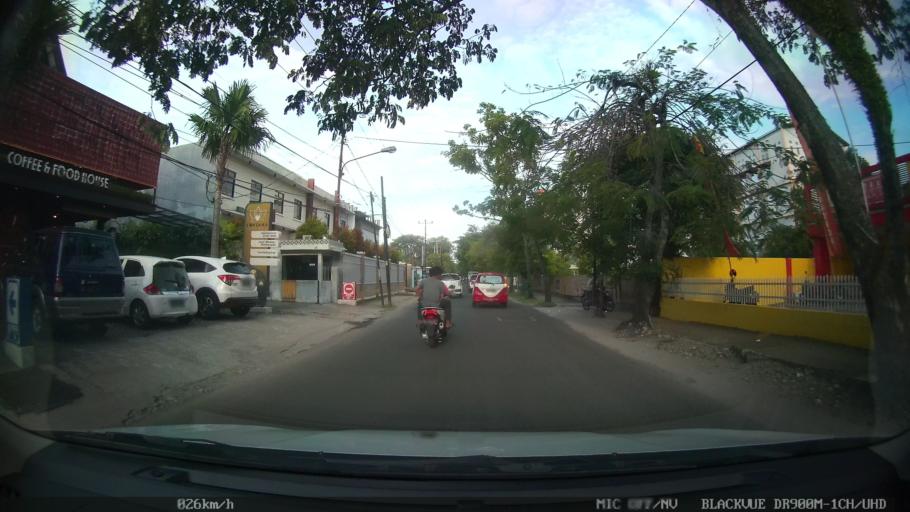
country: ID
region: North Sumatra
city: Medan
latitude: 3.5767
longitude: 98.6623
